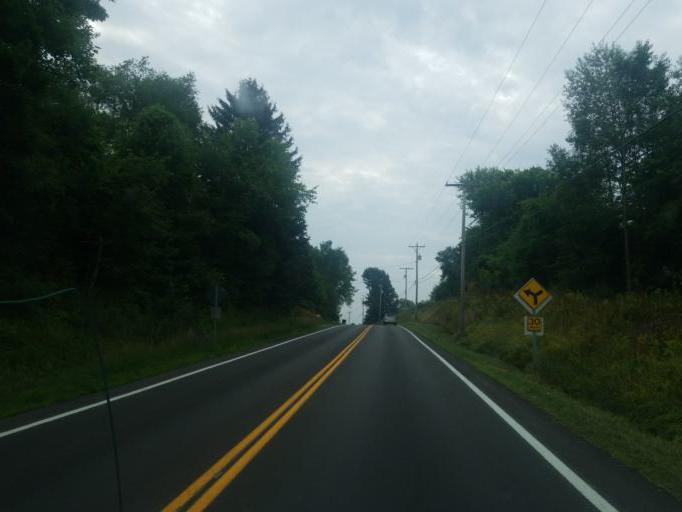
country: US
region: Ohio
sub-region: Stark County
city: Canton
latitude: 40.7728
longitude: -81.3452
